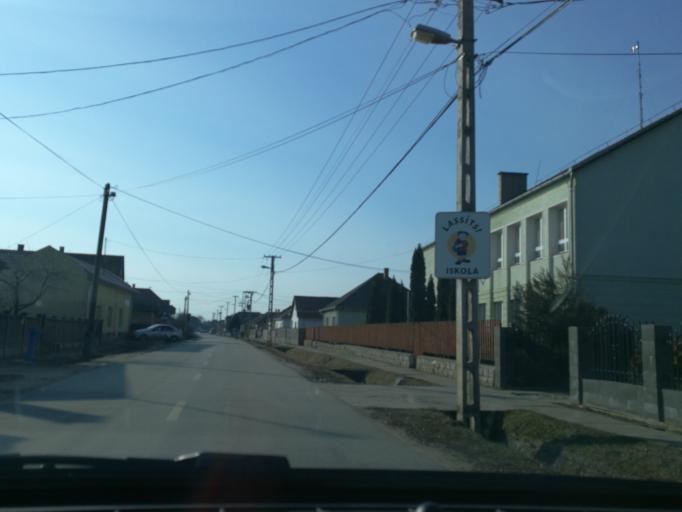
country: HU
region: Szabolcs-Szatmar-Bereg
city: Apagy
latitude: 48.0213
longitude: 21.9609
